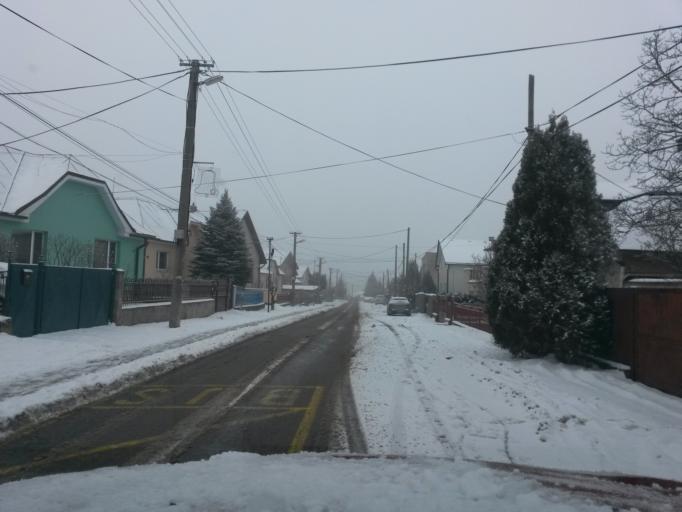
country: SK
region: Kosicky
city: Kosice
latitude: 48.7308
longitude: 21.3014
